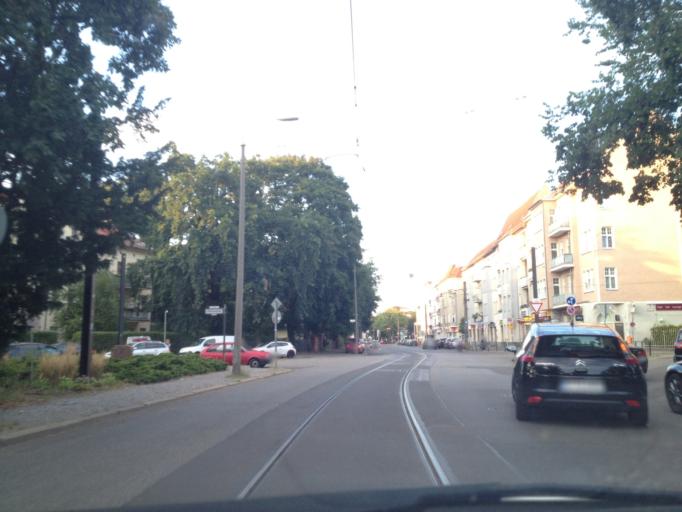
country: DE
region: Berlin
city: Johannisthal
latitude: 52.4455
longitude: 13.5037
